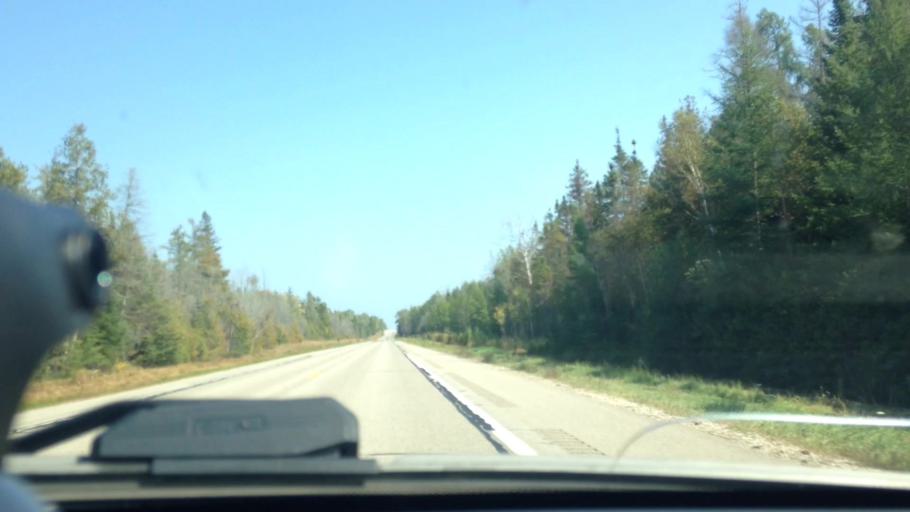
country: US
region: Michigan
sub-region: Luce County
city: Newberry
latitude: 46.3036
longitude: -85.3088
